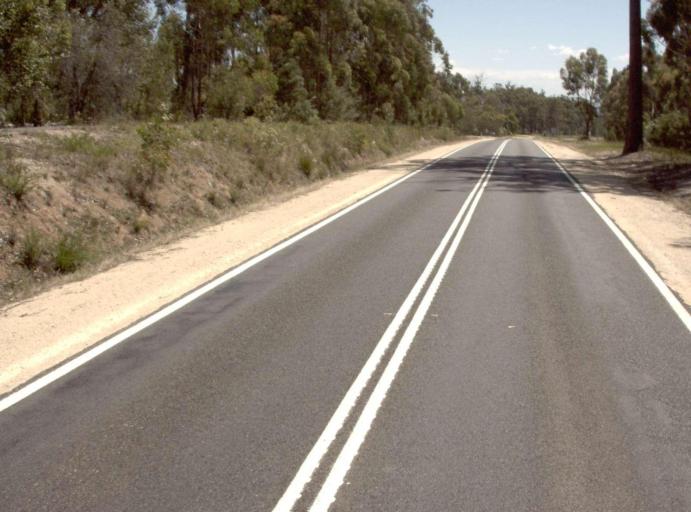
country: AU
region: New South Wales
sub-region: Bombala
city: Bombala
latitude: -37.5641
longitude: 149.1696
